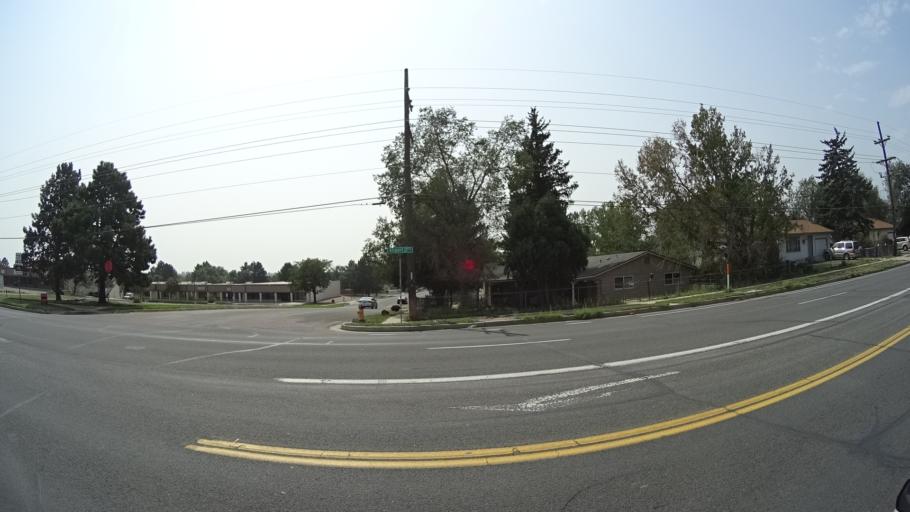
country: US
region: Colorado
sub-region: El Paso County
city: Colorado Springs
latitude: 38.8254
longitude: -104.7836
